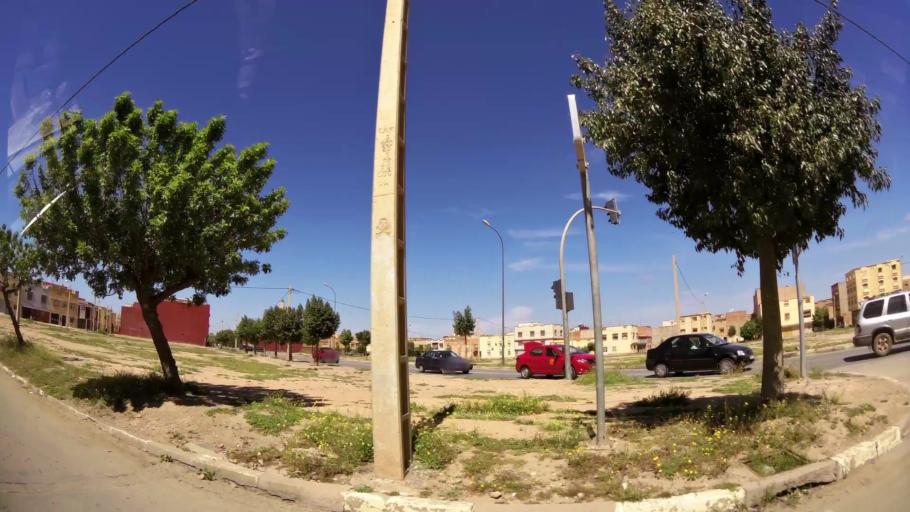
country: MA
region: Oriental
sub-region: Oujda-Angad
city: Oujda
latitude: 34.6661
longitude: -1.9272
